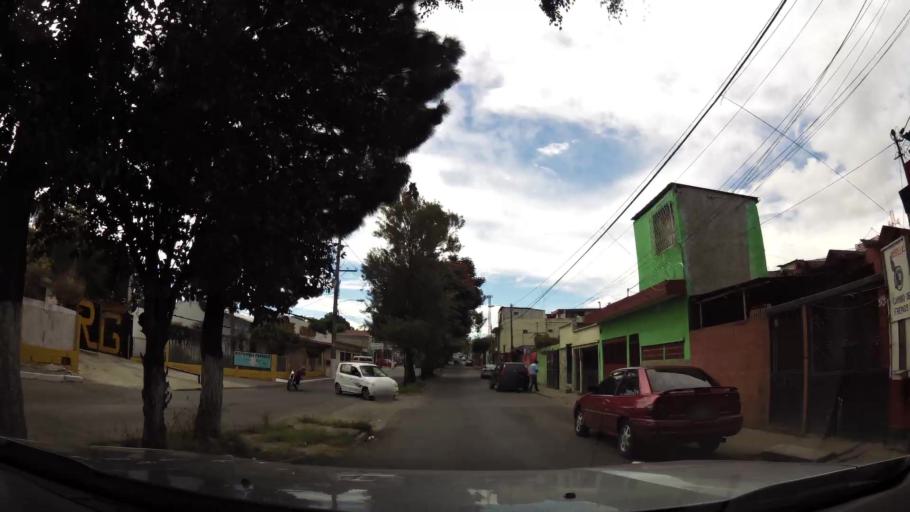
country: GT
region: Guatemala
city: Mixco
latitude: 14.6642
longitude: -90.5699
